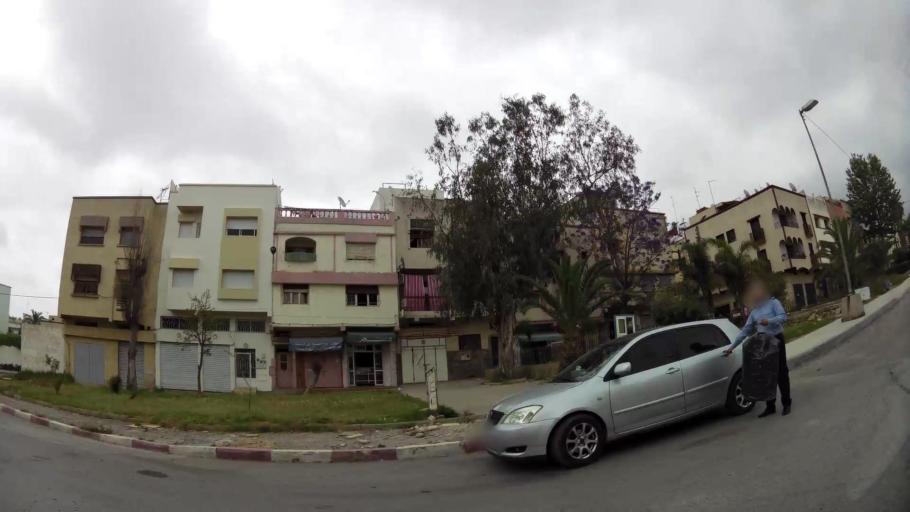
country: MA
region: Rabat-Sale-Zemmour-Zaer
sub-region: Rabat
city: Rabat
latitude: 33.9995
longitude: -6.8178
